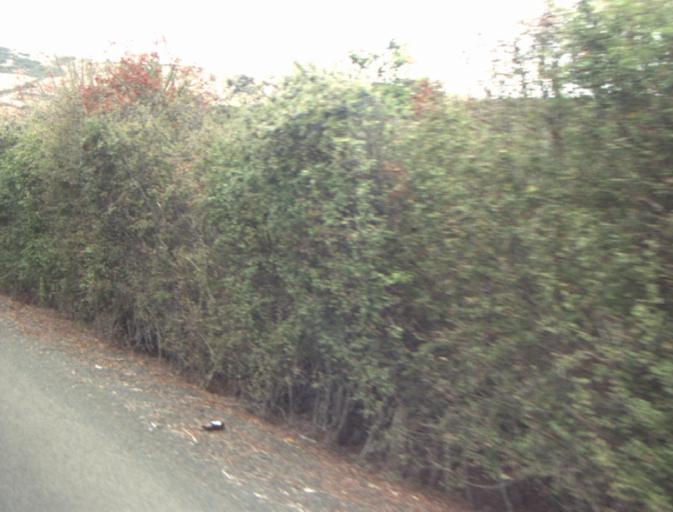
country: AU
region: Tasmania
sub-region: Northern Midlands
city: Evandale
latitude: -41.5285
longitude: 147.2447
